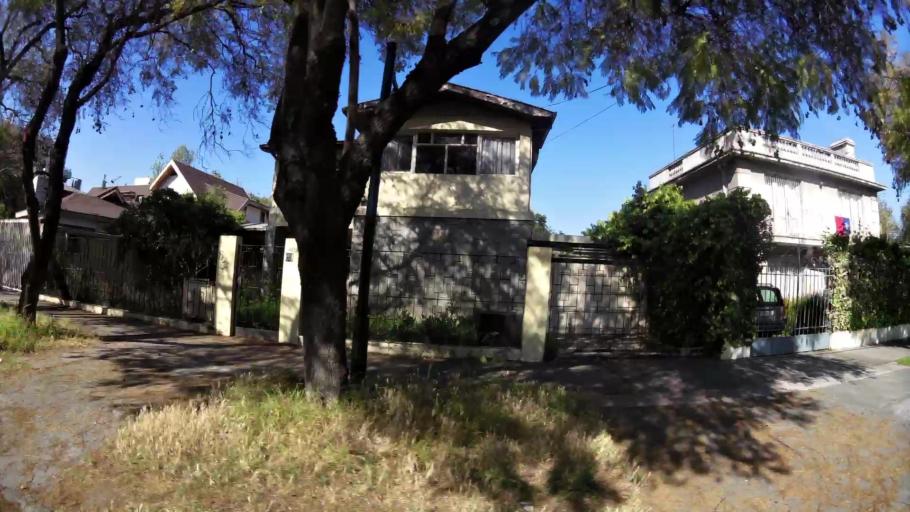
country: CL
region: Santiago Metropolitan
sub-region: Provincia de Santiago
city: Villa Presidente Frei, Nunoa, Santiago, Chile
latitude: -33.4380
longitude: -70.5843
